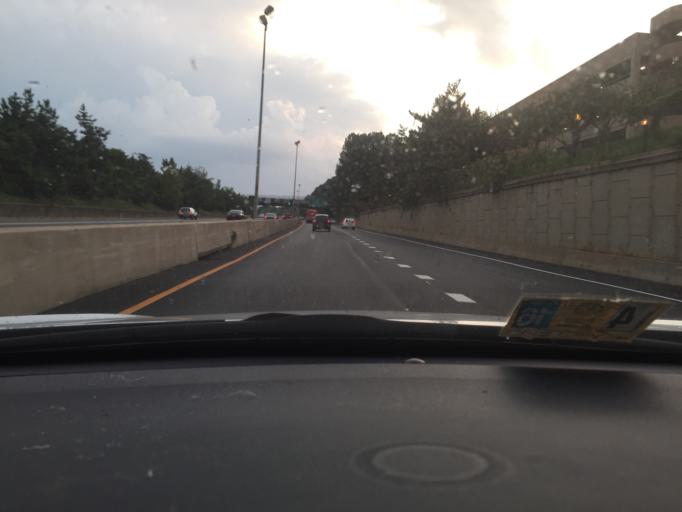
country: US
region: Virginia
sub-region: Fairfax County
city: Vienna
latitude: 38.8781
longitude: -77.2716
